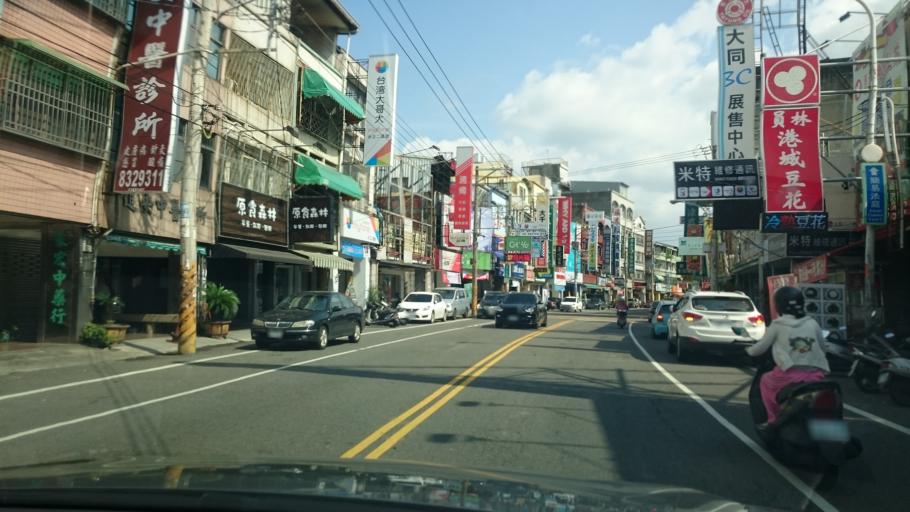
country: TW
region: Taiwan
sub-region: Nantou
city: Nantou
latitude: 23.9525
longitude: 120.5755
